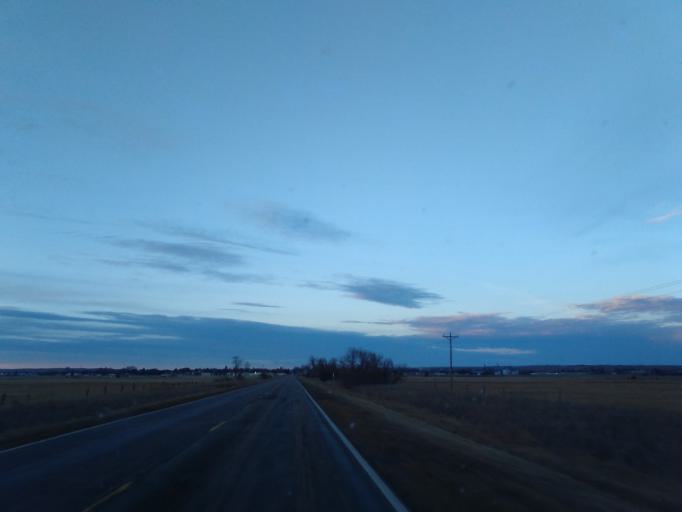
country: US
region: Nebraska
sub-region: Garden County
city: Oshkosh
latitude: 41.3884
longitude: -102.3476
